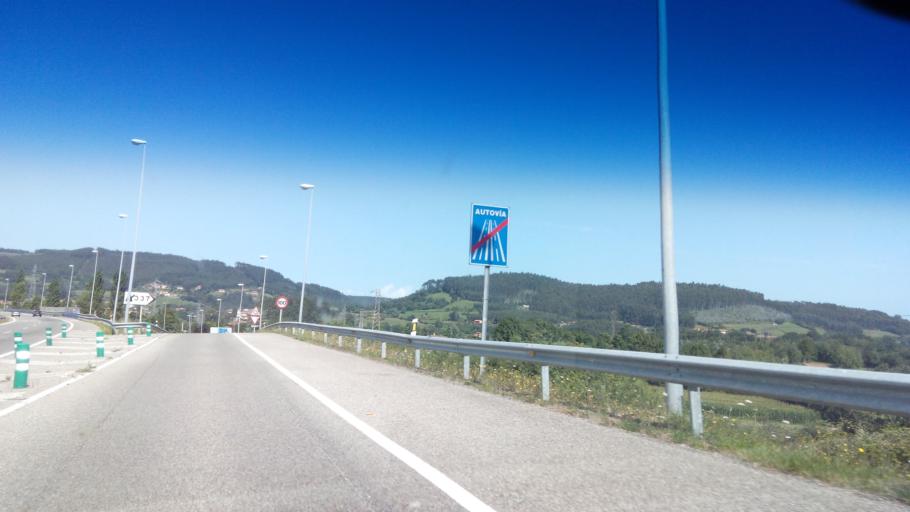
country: ES
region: Asturias
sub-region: Province of Asturias
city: Colunga
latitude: 43.4784
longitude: -5.2523
